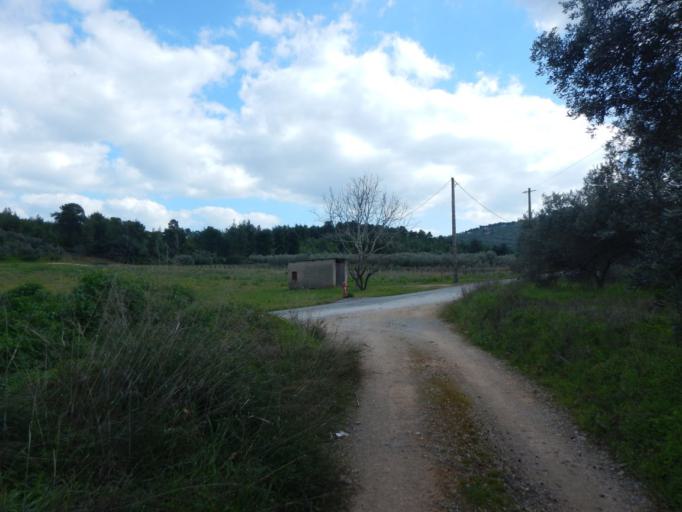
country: GR
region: Attica
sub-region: Nomarchia Anatolikis Attikis
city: Markopoulo Oropou
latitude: 38.2969
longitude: 23.8405
